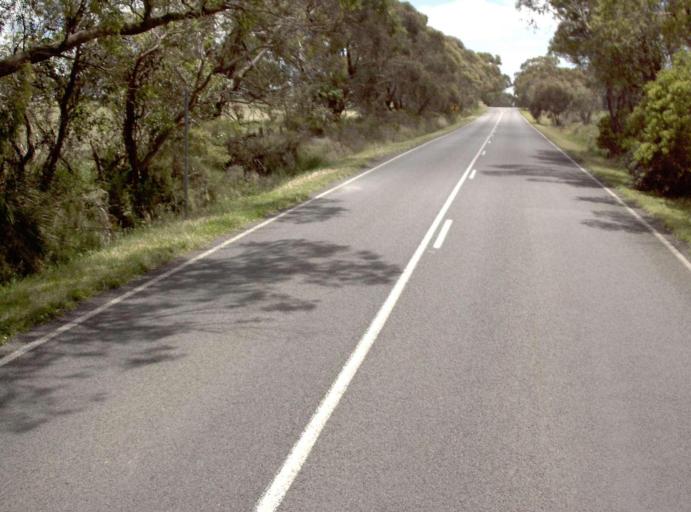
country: AU
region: Victoria
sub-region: Bass Coast
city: North Wonthaggi
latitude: -38.6130
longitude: 146.0166
